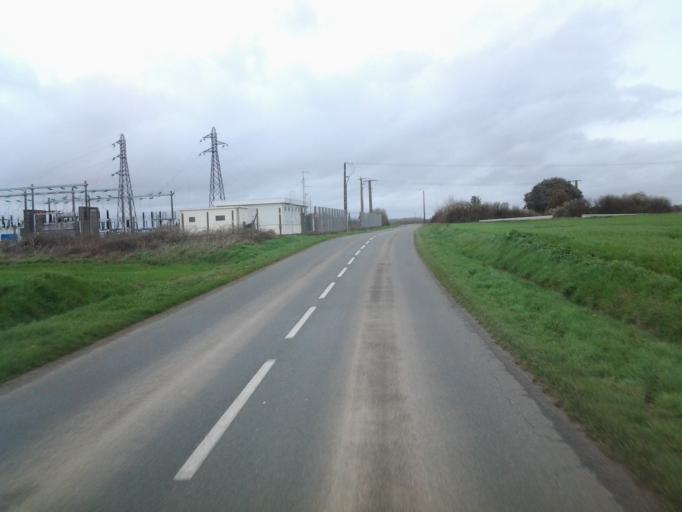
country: FR
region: Pays de la Loire
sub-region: Departement de la Vendee
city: Longeville-sur-Mer
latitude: 46.4321
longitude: -1.4882
